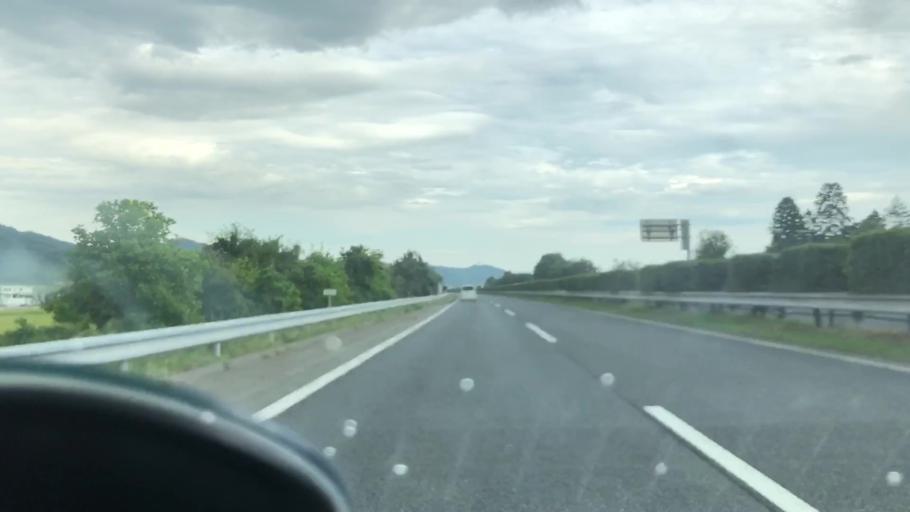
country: JP
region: Hyogo
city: Ono
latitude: 34.9434
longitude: 134.8114
